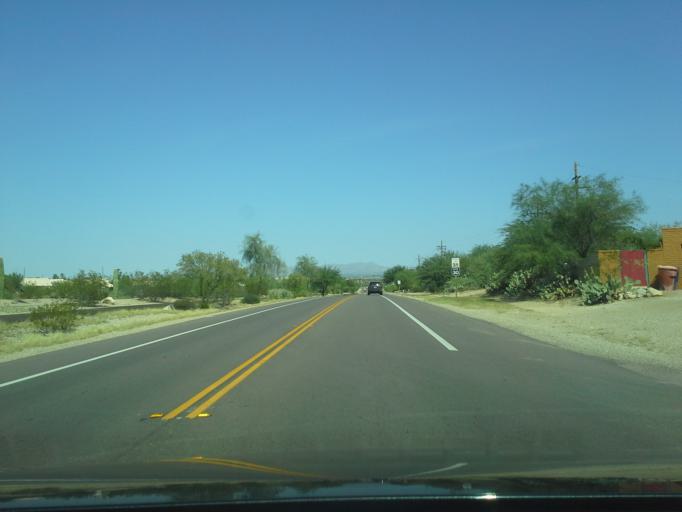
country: US
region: Arizona
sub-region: Pima County
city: Flowing Wells
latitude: 32.2445
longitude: -111.0205
